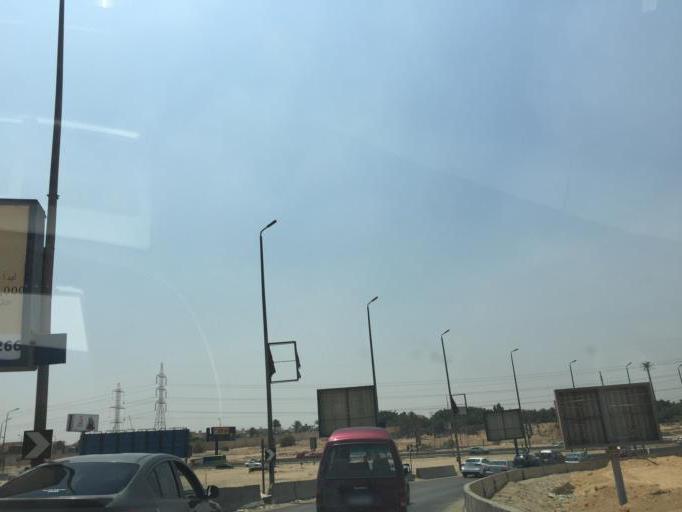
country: EG
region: Muhafazat al Qalyubiyah
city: Al Khankah
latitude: 30.0812
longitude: 31.4376
